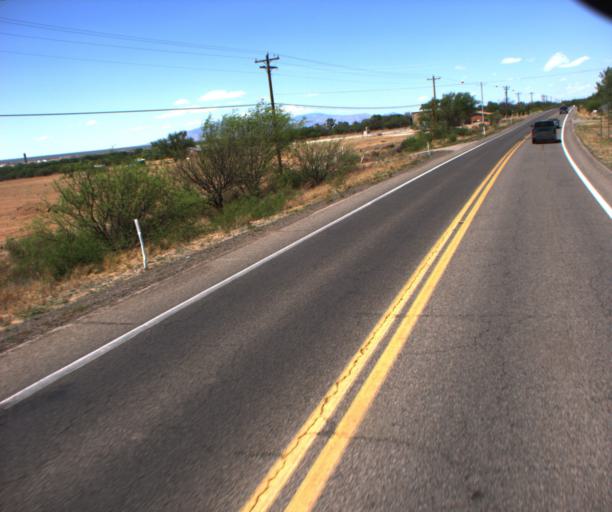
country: US
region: Arizona
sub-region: Cochise County
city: Saint David
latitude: 31.8670
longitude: -110.2073
